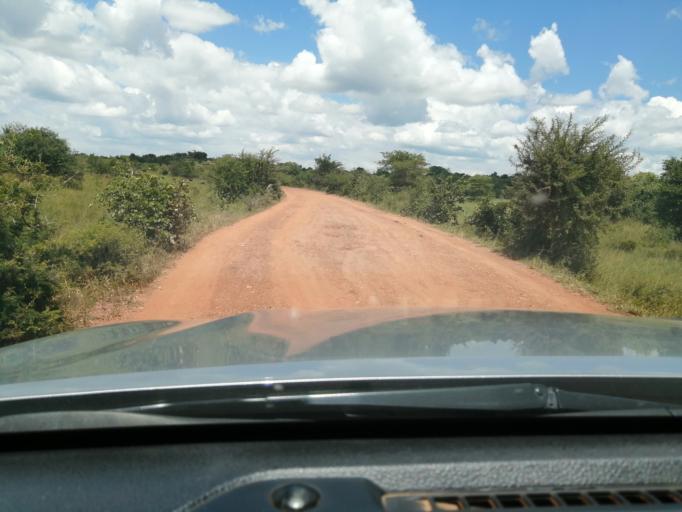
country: ZM
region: Lusaka
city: Lusaka
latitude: -15.1786
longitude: 27.9472
